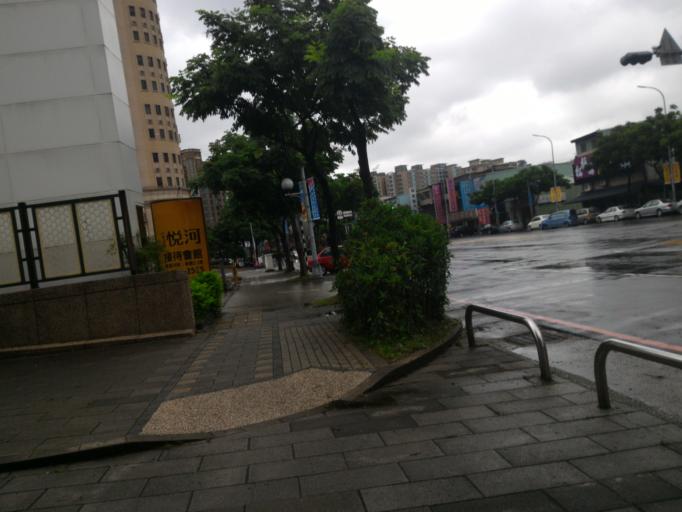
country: TW
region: Taiwan
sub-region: Taoyuan
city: Taoyuan
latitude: 24.9412
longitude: 121.3785
